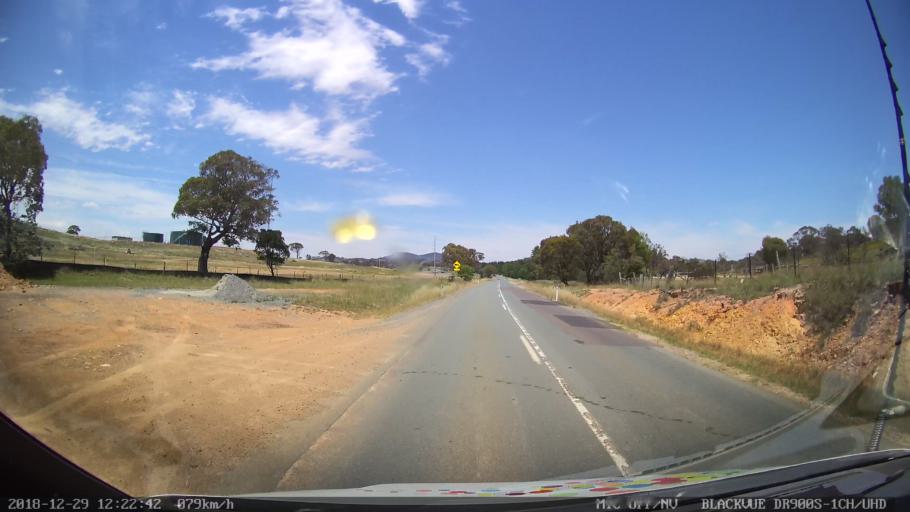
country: AU
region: New South Wales
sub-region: Queanbeyan
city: Queanbeyan
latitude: -35.4279
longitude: 149.2198
